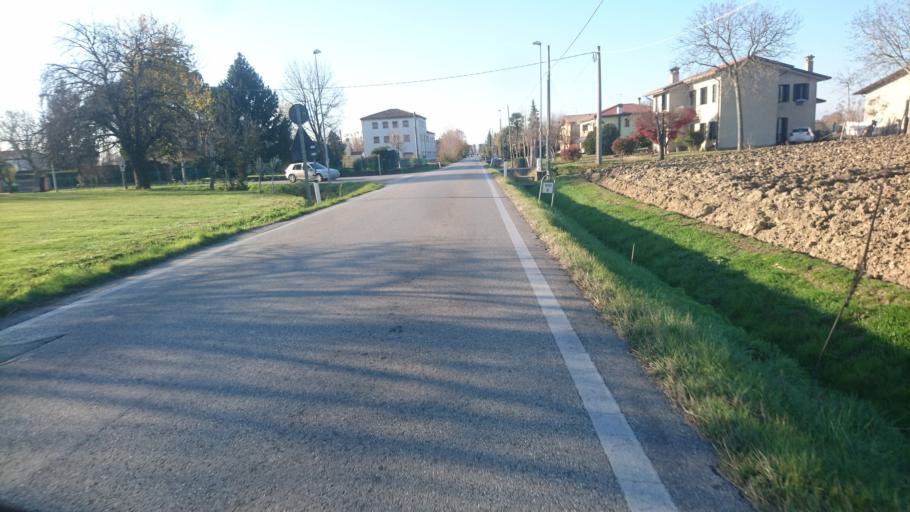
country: IT
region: Veneto
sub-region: Provincia di Padova
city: Rubano
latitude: 45.4218
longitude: 11.7704
